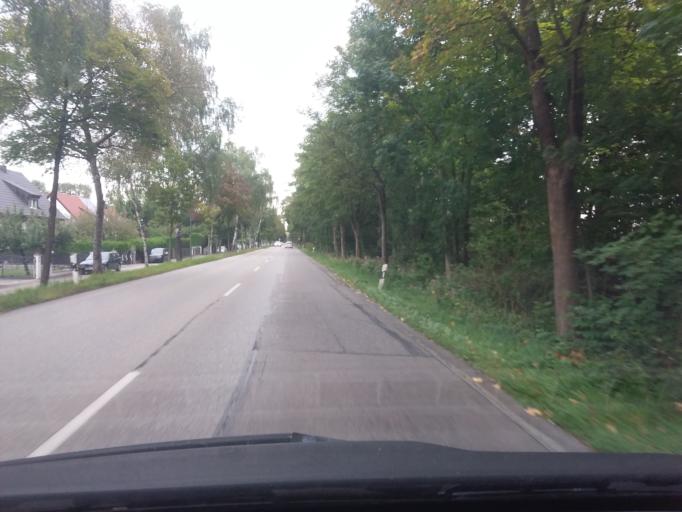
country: DE
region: Bavaria
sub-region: Upper Bavaria
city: Hebertshausen
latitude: 48.2556
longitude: 11.4766
